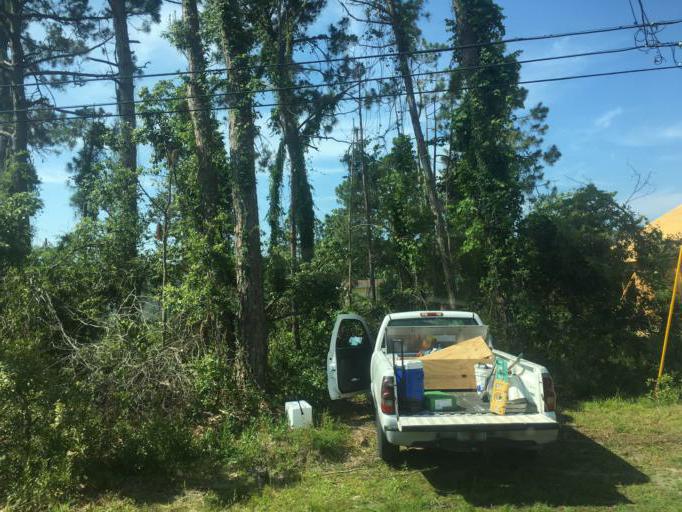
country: US
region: Florida
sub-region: Bay County
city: Upper Grand Lagoon
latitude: 30.1620
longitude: -85.7562
